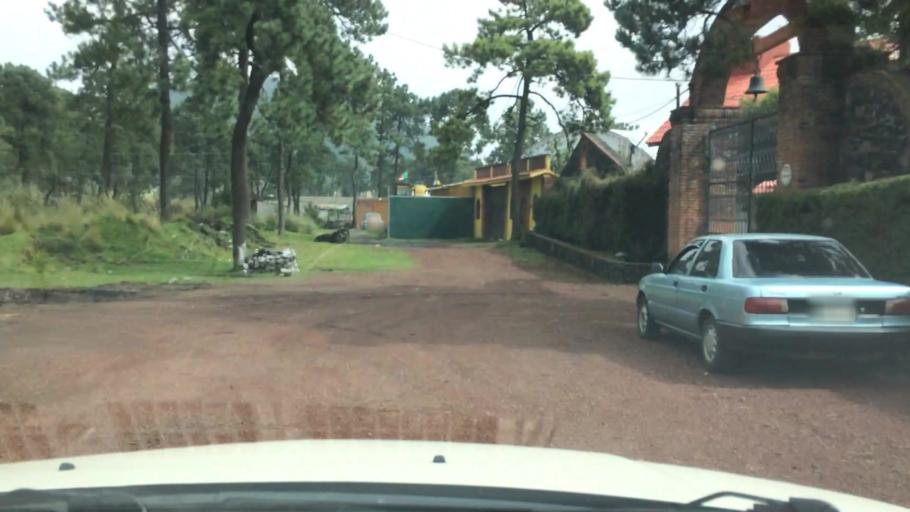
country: MX
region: Mexico City
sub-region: Tlalpan
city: Lomas de Tepemecatl
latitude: 19.2345
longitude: -99.2222
